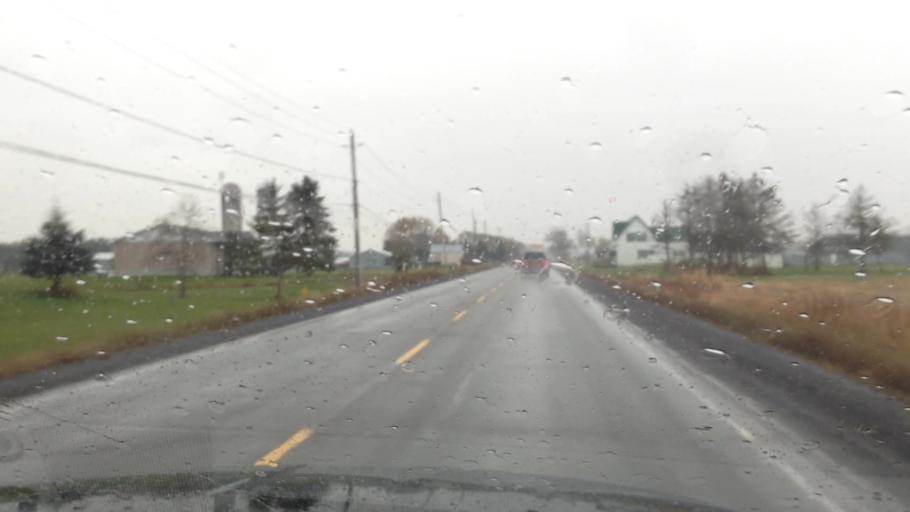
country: CA
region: Ontario
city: Bourget
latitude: 45.3133
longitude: -75.3359
